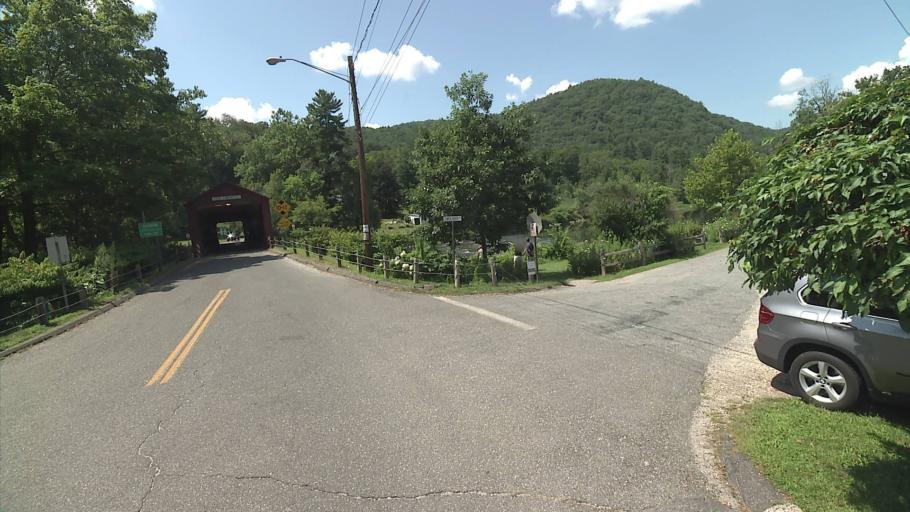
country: US
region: Connecticut
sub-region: Litchfield County
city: Canaan
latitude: 41.8716
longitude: -73.3631
